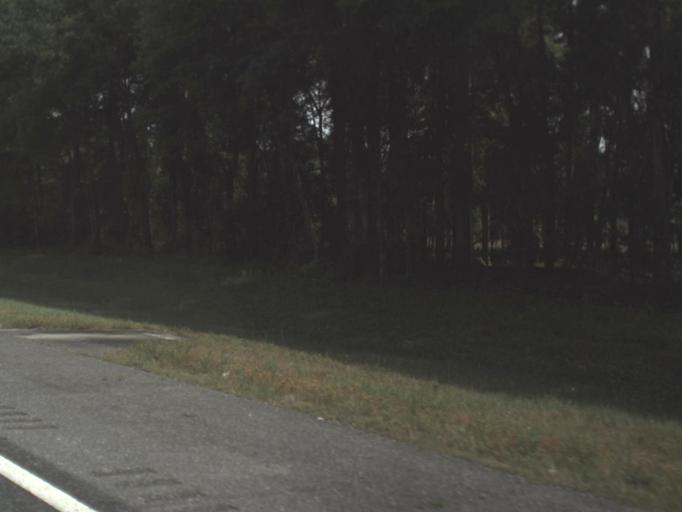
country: US
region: Florida
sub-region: Suwannee County
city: Live Oak
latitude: 30.2990
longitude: -82.9063
